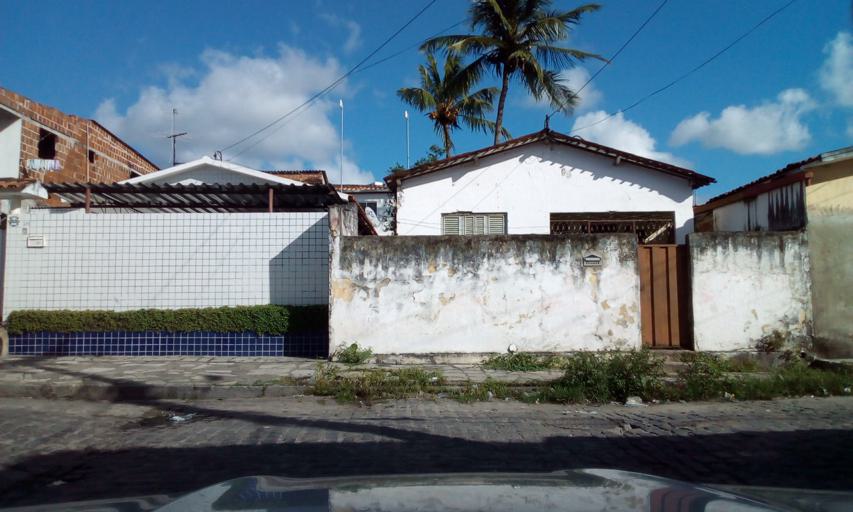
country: BR
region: Paraiba
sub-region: Joao Pessoa
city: Joao Pessoa
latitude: -7.1047
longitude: -34.8670
